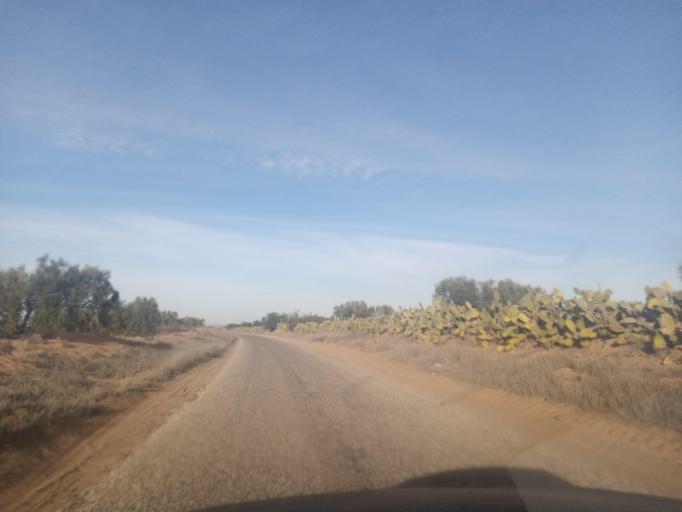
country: TN
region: Safaqis
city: Bi'r `Ali Bin Khalifah
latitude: 34.8774
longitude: 10.1705
